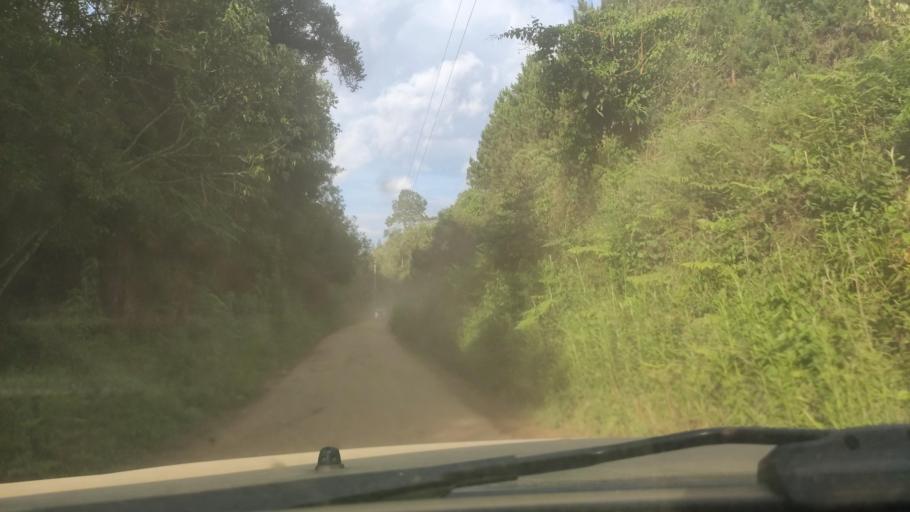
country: BR
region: Minas Gerais
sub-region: Cambui
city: Cambui
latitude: -22.7523
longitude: -45.9352
